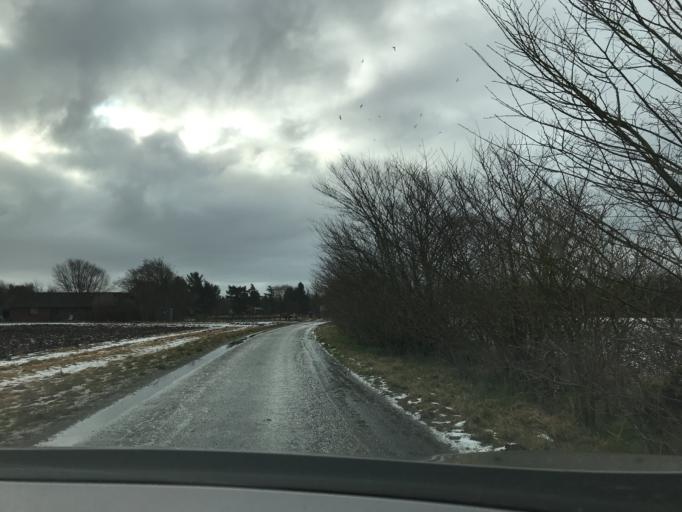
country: DK
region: South Denmark
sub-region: Varde Kommune
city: Oksbol
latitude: 55.7629
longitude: 8.2705
